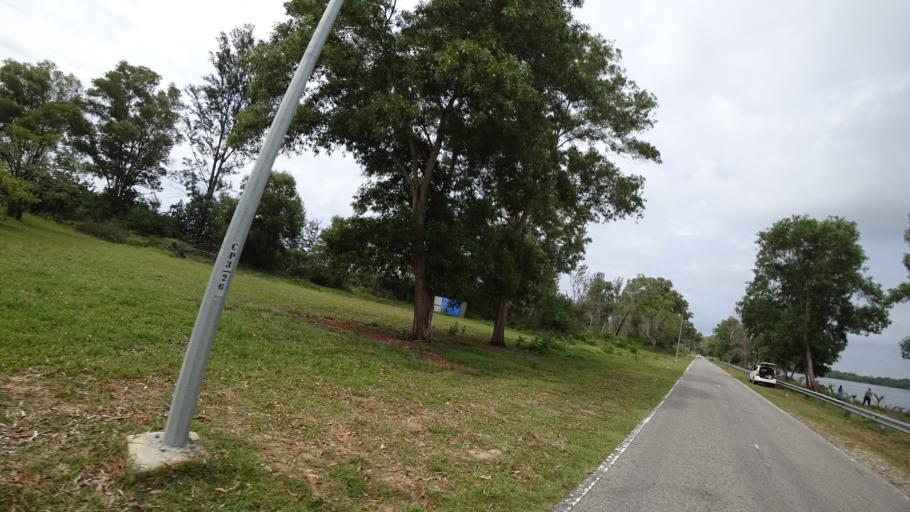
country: BN
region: Tutong
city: Tutong
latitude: 4.7859
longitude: 114.6129
